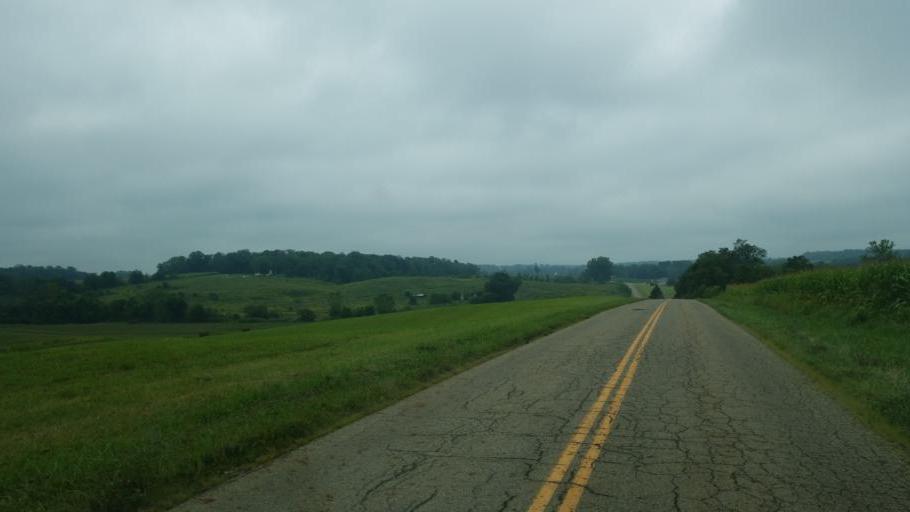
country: US
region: Ohio
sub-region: Licking County
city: Utica
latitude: 40.2683
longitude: -82.4153
